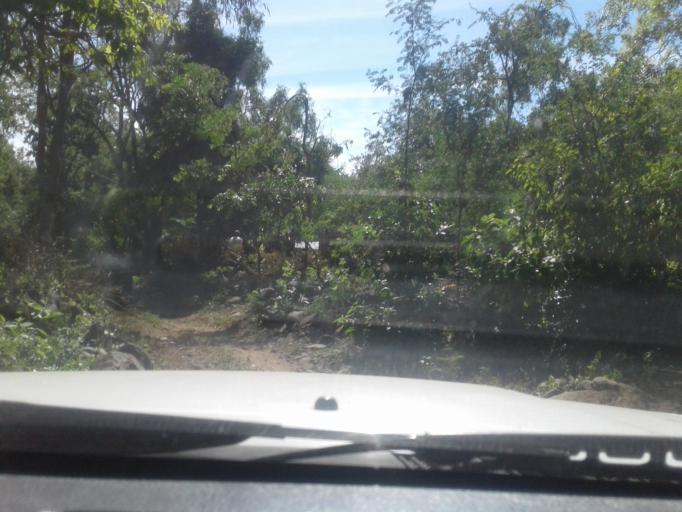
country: NI
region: Carazo
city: Santa Teresa
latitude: 11.5980
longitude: -86.2145
